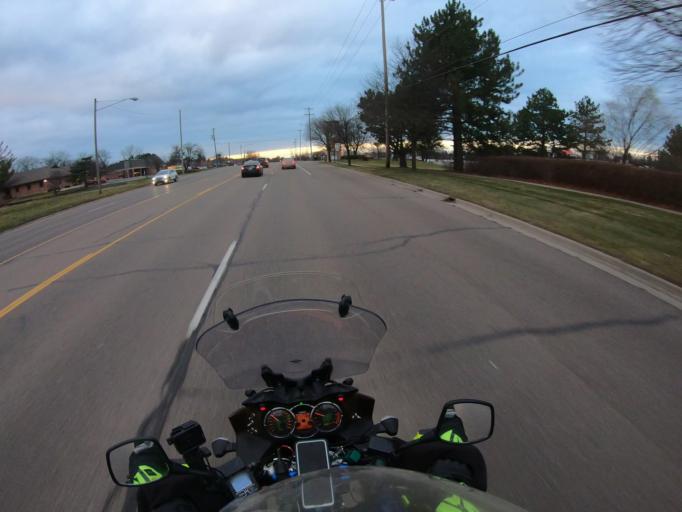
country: US
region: Michigan
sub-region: Genesee County
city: Grand Blanc
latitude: 42.9177
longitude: -83.6155
